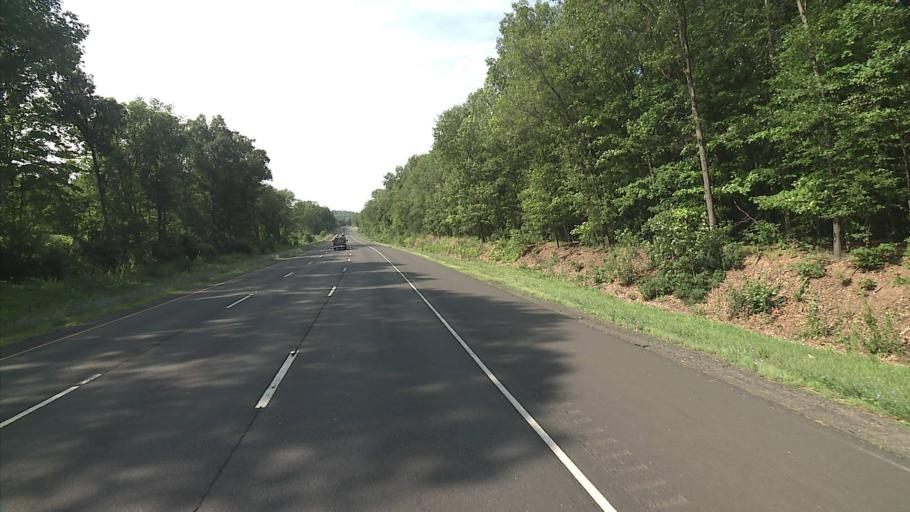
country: US
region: Connecticut
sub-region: Middlesex County
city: Cromwell
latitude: 41.5971
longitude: -72.7088
